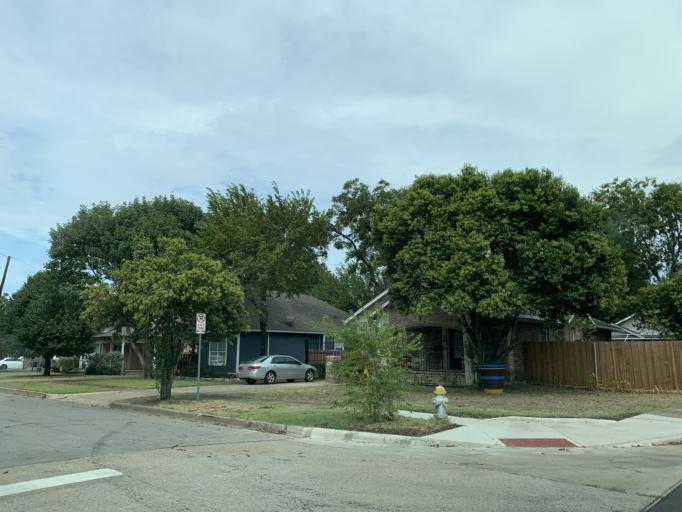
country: US
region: Texas
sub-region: Dallas County
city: Cockrell Hill
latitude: 32.7413
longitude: -96.8503
